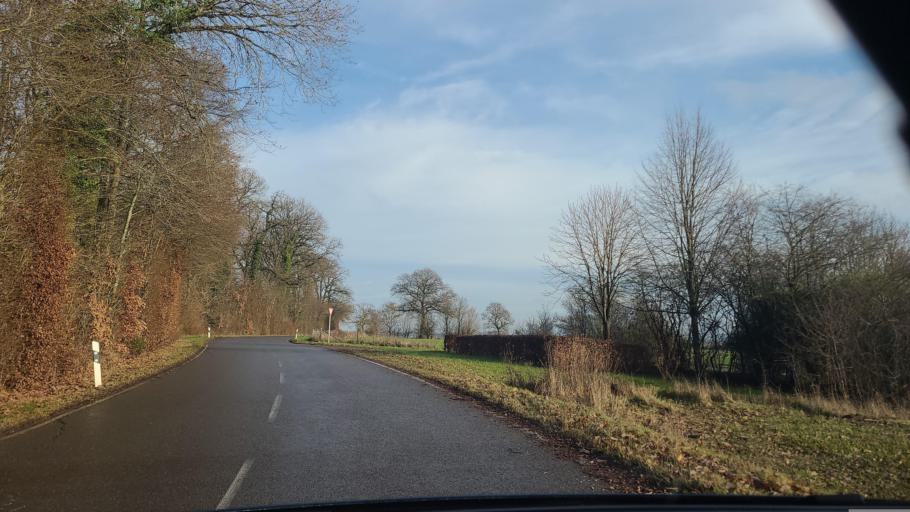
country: LU
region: Luxembourg
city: Capellen
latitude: 49.6535
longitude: 5.9713
